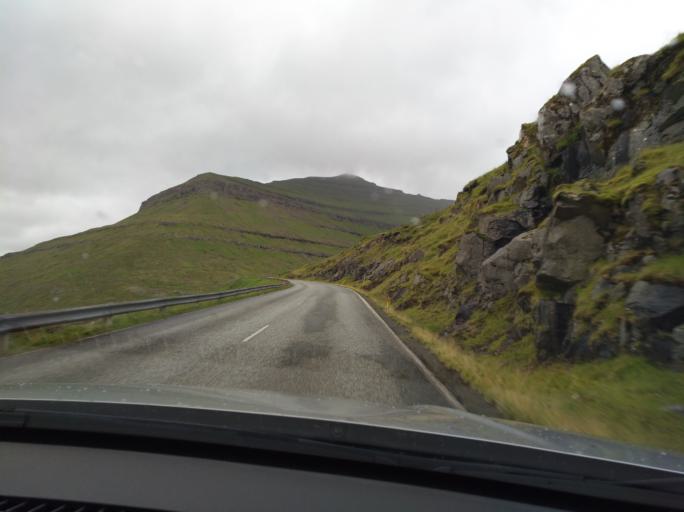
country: FO
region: Eysturoy
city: Fuglafjordur
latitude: 62.2208
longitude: -6.8718
